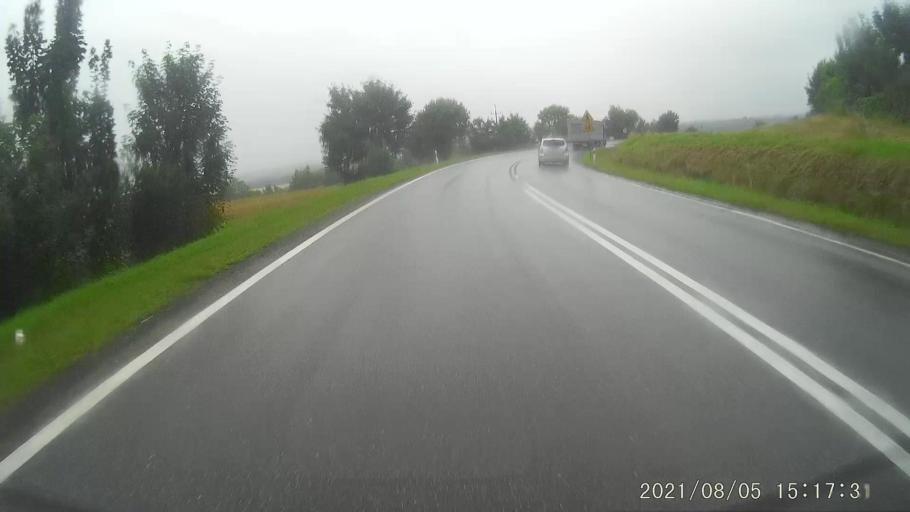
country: PL
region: Lower Silesian Voivodeship
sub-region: Powiat zabkowicki
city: Zloty Stok
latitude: 50.4553
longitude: 16.8482
